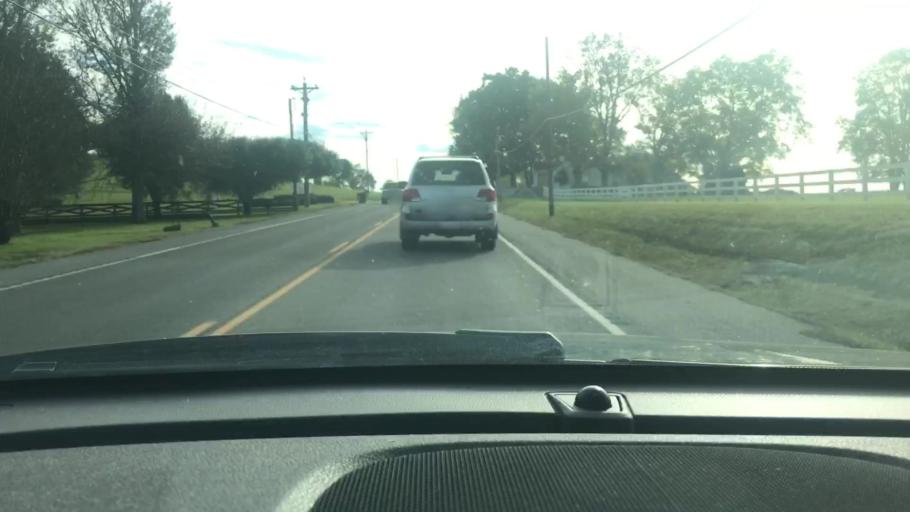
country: US
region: Tennessee
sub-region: Williamson County
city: Franklin
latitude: 35.9381
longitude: -86.8584
